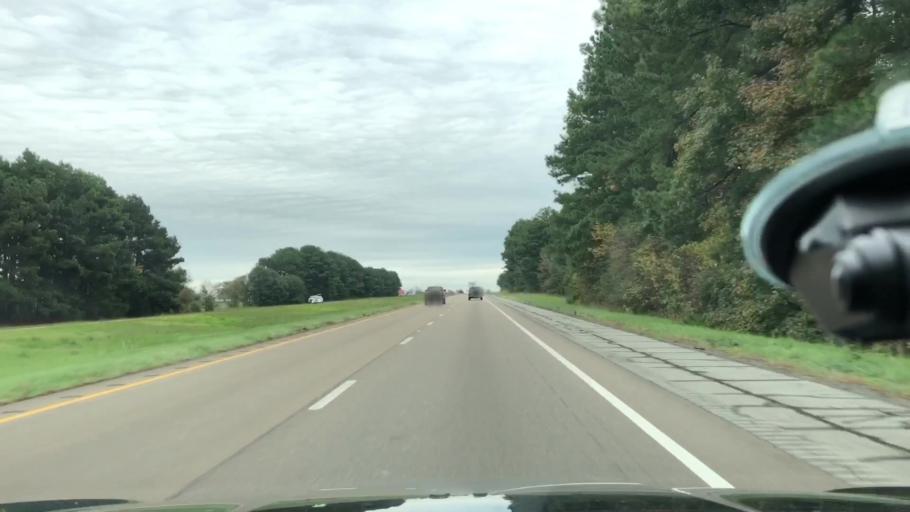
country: US
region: Texas
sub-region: Morris County
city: Omaha
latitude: 33.2825
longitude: -94.7942
